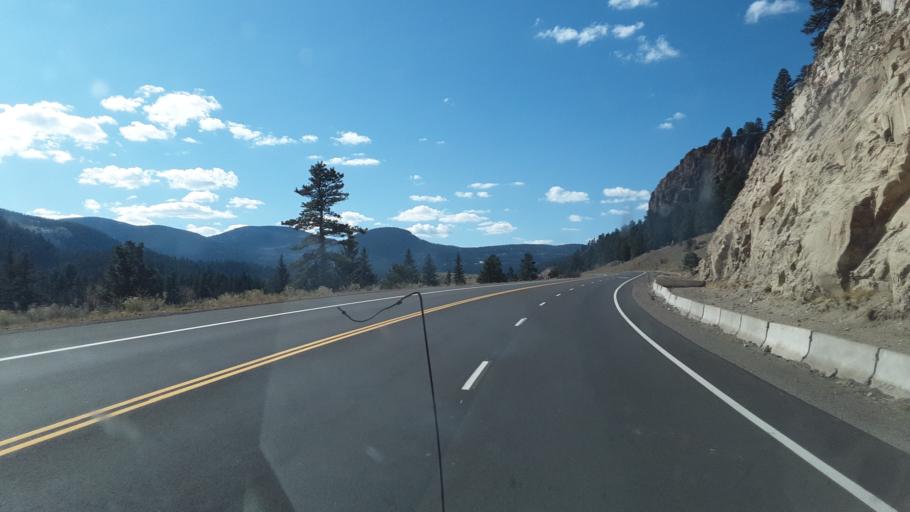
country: US
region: Colorado
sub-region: Rio Grande County
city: Del Norte
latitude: 37.6428
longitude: -106.6633
